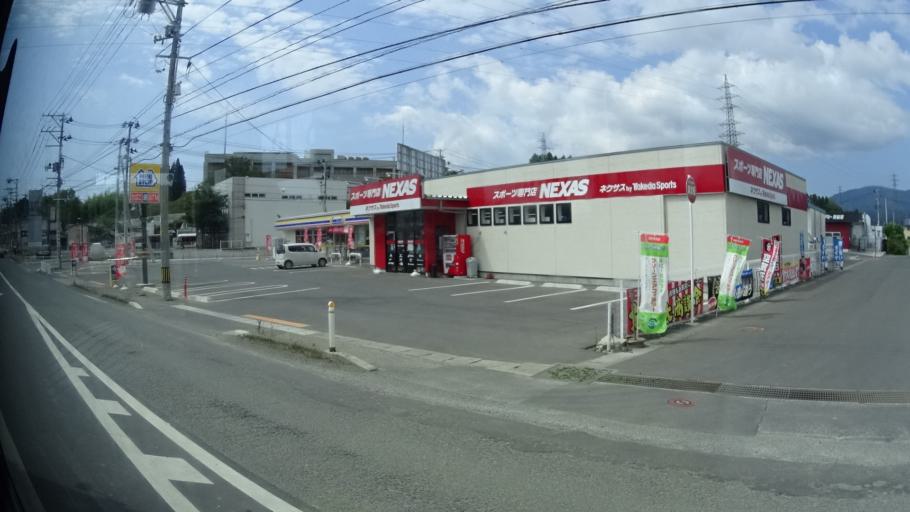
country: JP
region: Iwate
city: Ofunato
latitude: 38.8898
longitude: 141.5703
